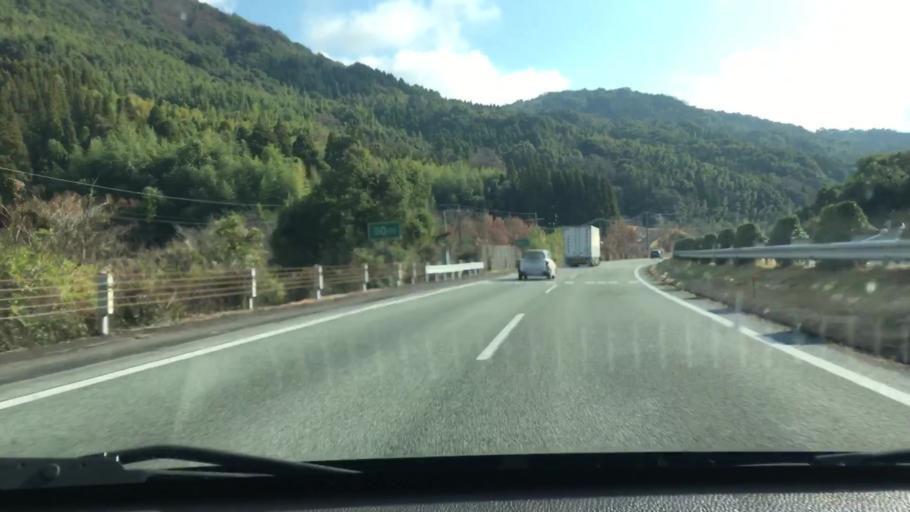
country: JP
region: Kumamoto
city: Matsubase
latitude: 32.6139
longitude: 130.7240
